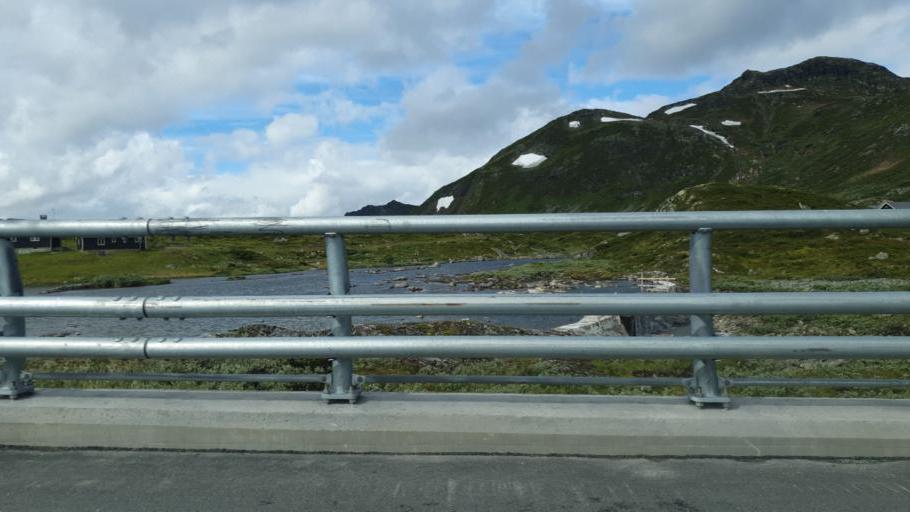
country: NO
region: Oppland
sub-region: Vestre Slidre
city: Slidre
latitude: 61.3296
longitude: 8.7987
